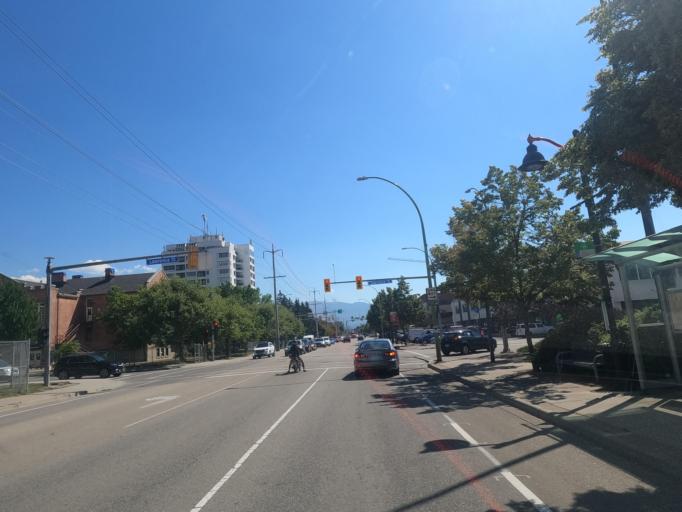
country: CA
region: British Columbia
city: Kelowna
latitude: 49.8857
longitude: -119.4886
